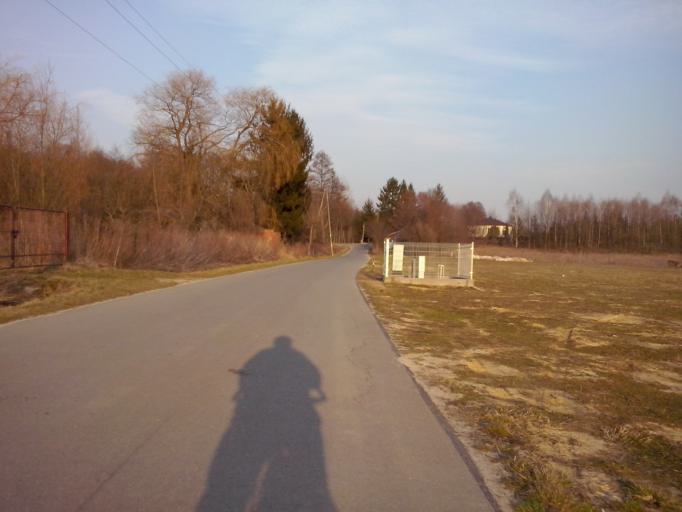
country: PL
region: Subcarpathian Voivodeship
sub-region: Powiat nizanski
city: Krzeszow
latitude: 50.4016
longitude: 22.3483
